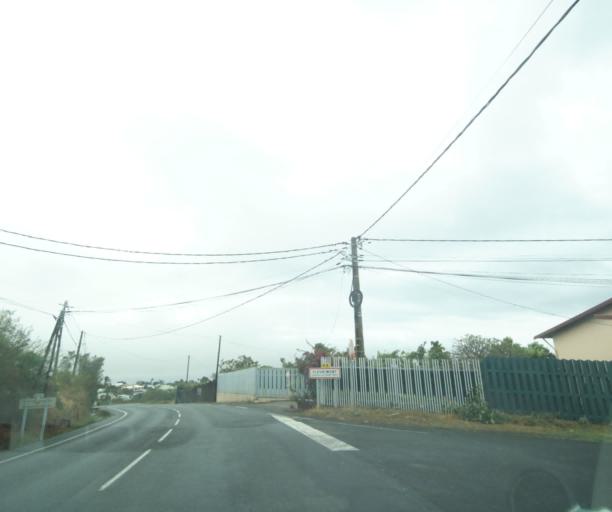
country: RE
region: Reunion
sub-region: Reunion
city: Saint-Paul
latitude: -21.0344
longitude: 55.2745
